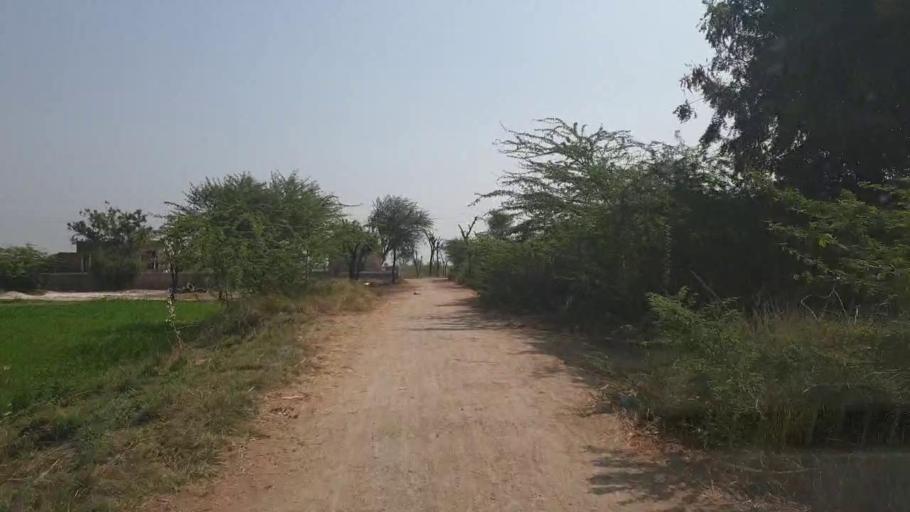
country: PK
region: Sindh
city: Dhoro Naro
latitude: 25.4872
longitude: 69.5368
